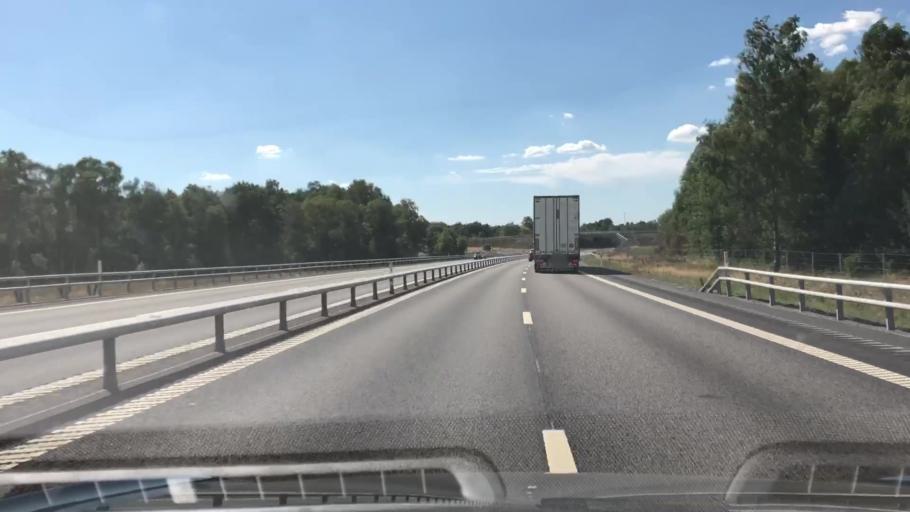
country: SE
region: Skane
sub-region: Horby Kommun
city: Hoerby
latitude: 55.9272
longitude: 13.8301
